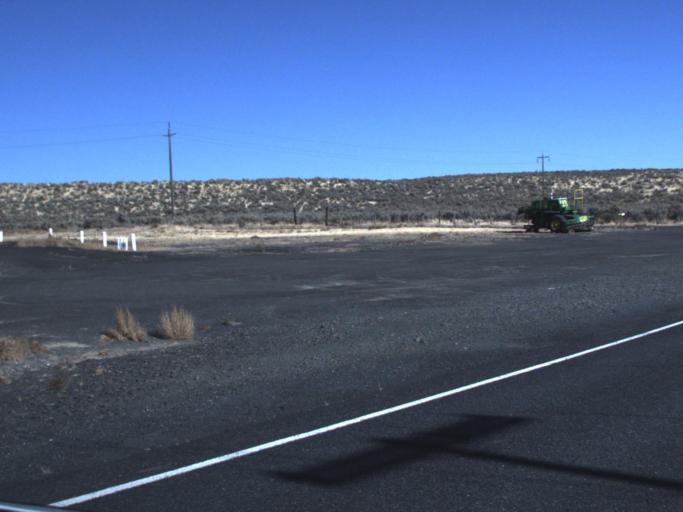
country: US
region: Washington
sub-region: Adams County
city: Ritzville
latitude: 46.9702
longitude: -118.5896
